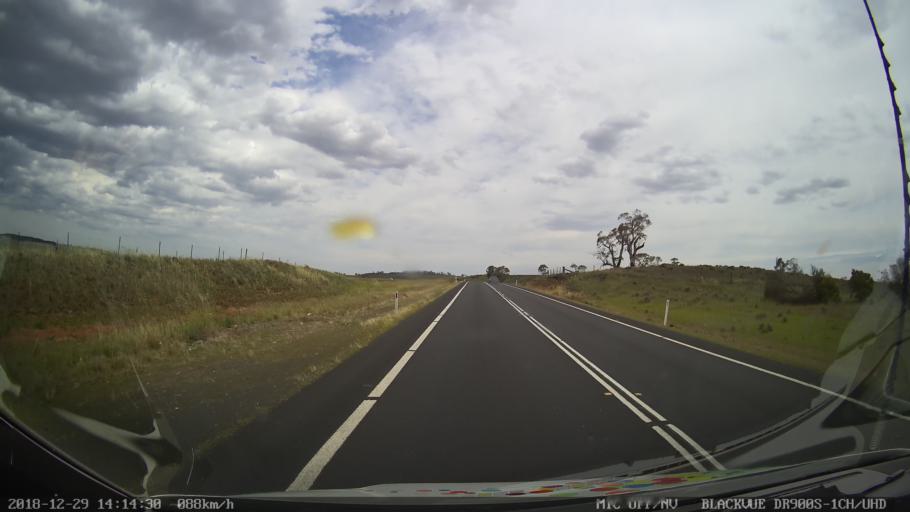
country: AU
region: New South Wales
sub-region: Cooma-Monaro
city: Cooma
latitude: -36.4433
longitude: 149.2373
